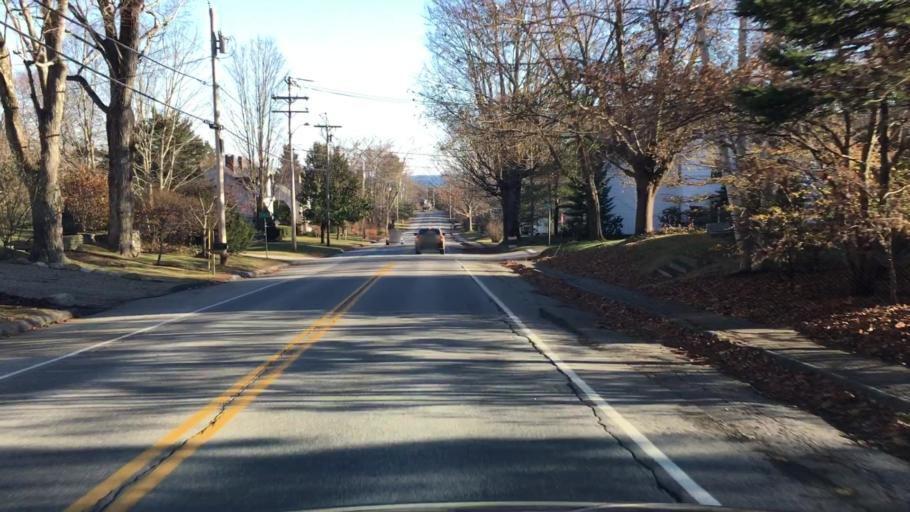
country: US
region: Maine
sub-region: Knox County
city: Camden
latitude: 44.2151
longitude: -69.0696
